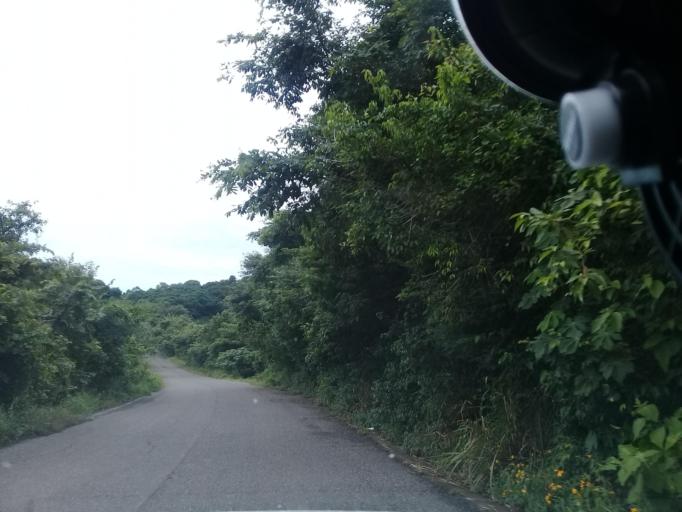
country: MX
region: Hidalgo
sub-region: Huejutla de Reyes
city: Chalahuiyapa
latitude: 21.2095
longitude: -98.3581
